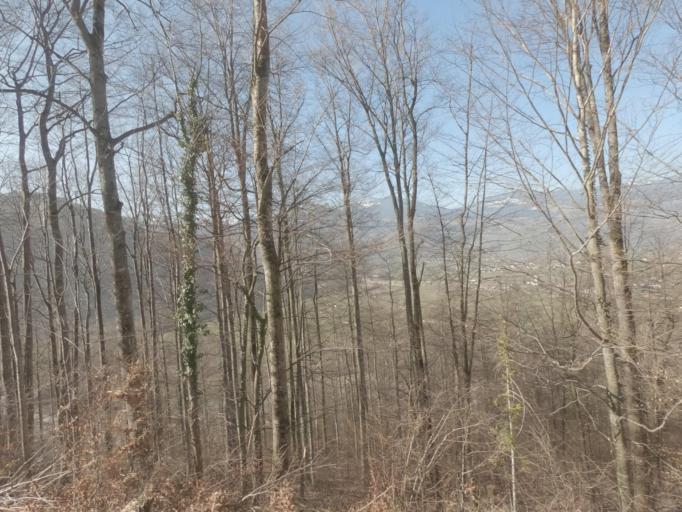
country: CH
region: Obwalden
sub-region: Obwalden
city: Giswil
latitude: 46.8221
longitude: 8.1831
